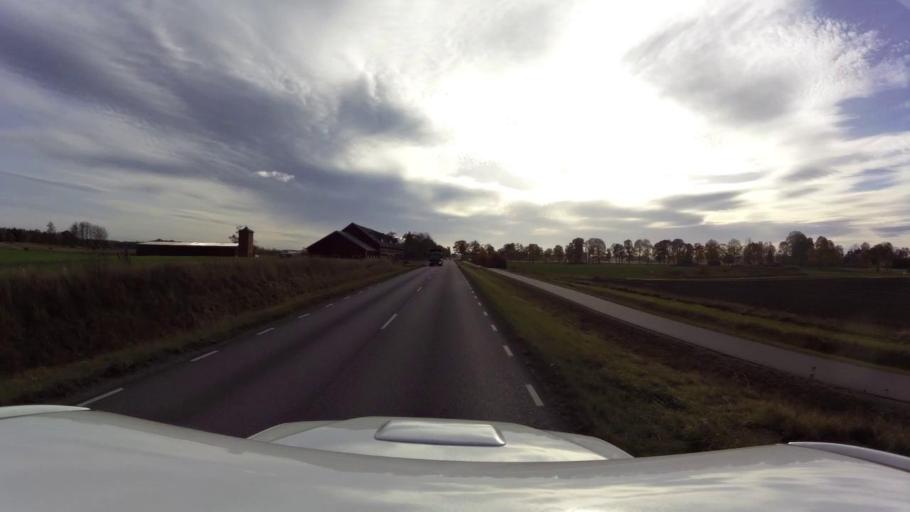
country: SE
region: OEstergoetland
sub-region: Linkopings Kommun
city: Ekangen
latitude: 58.4547
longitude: 15.6418
